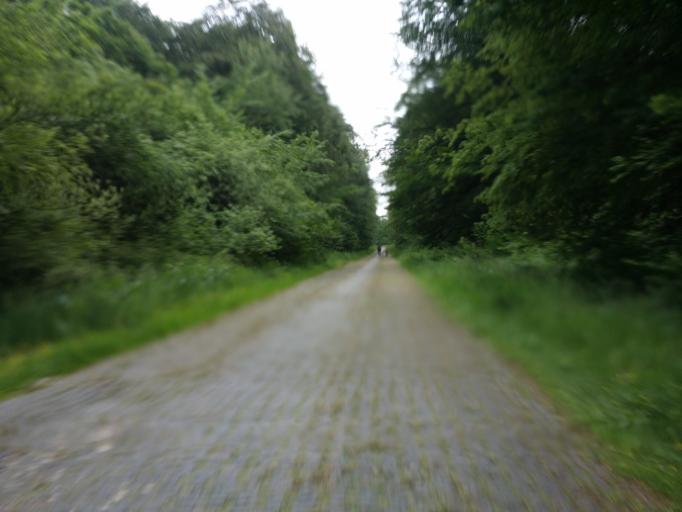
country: DE
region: Lower Saxony
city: Zetel
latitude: 53.3792
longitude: 7.9787
